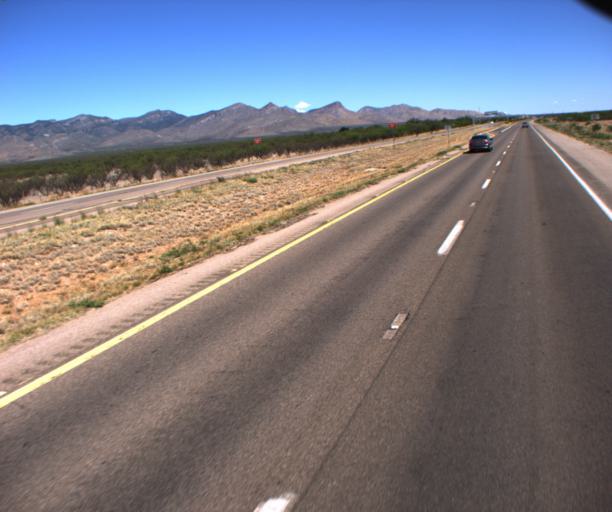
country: US
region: Arizona
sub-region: Cochise County
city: Huachuca City
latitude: 31.7171
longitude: -110.3502
